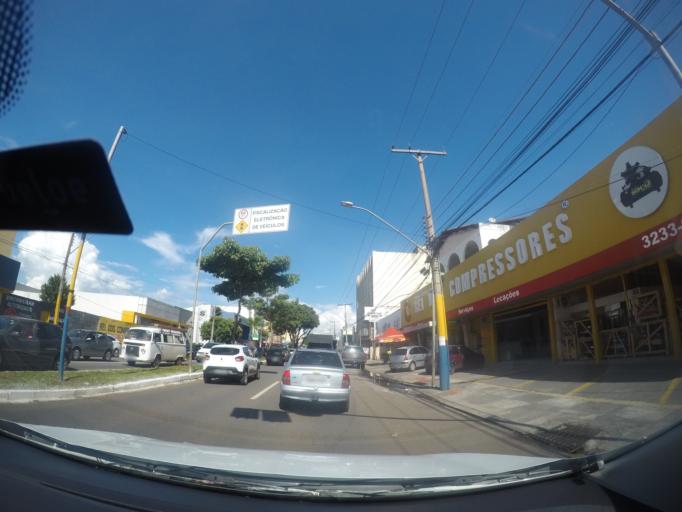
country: BR
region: Goias
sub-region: Goiania
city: Goiania
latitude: -16.6761
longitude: -49.2901
